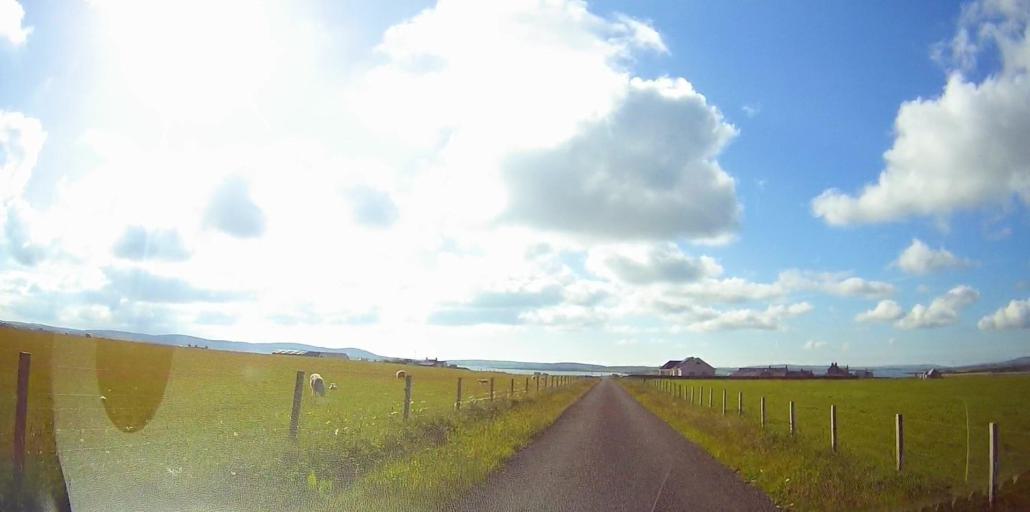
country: GB
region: Scotland
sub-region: Orkney Islands
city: Stromness
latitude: 58.9870
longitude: -3.1939
